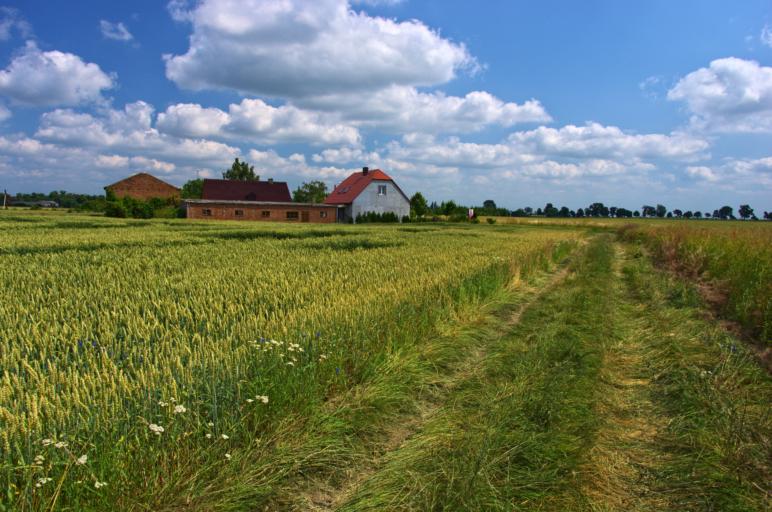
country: PL
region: Kujawsko-Pomorskie
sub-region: Powiat mogilenski
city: Strzelno
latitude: 52.6199
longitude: 18.1578
